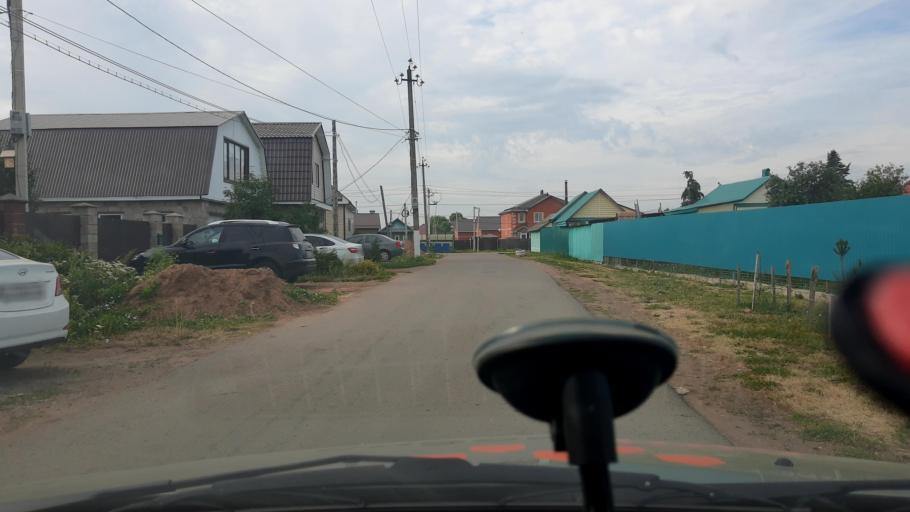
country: RU
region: Bashkortostan
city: Mikhaylovka
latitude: 54.7766
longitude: 55.8272
